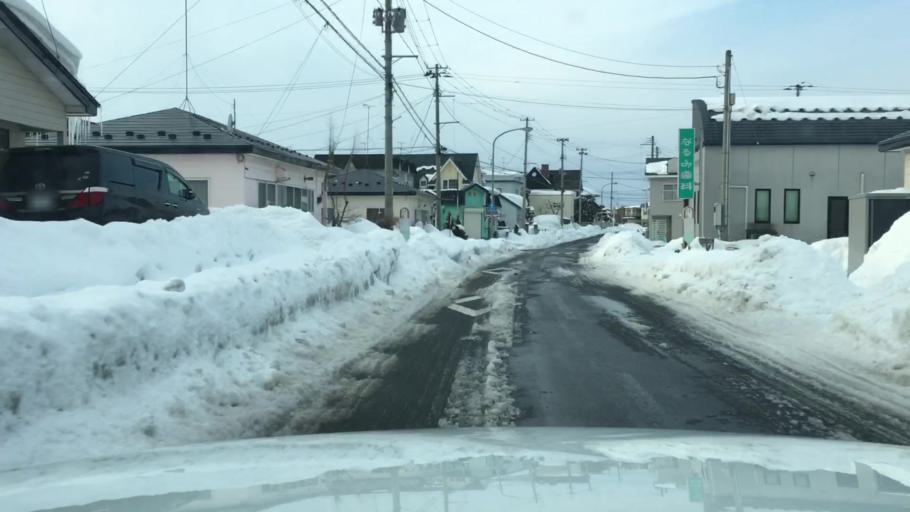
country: JP
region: Aomori
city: Hirosaki
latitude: 40.5772
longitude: 140.4895
